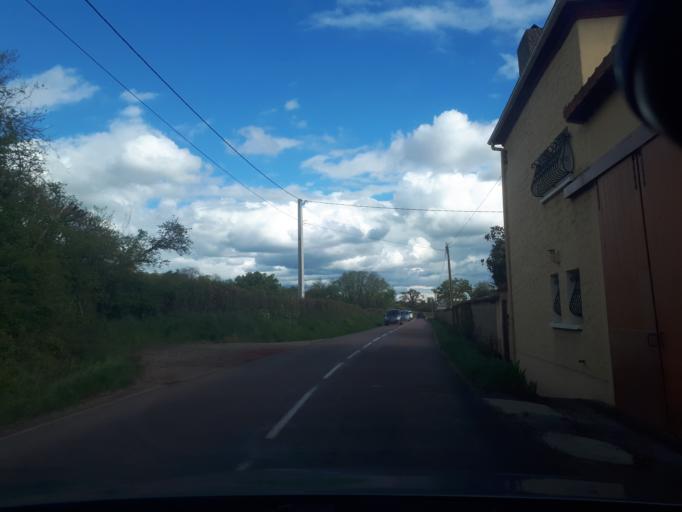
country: FR
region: Rhone-Alpes
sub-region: Departement de la Loire
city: Pouilly-les-Feurs
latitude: 45.8070
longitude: 4.2233
